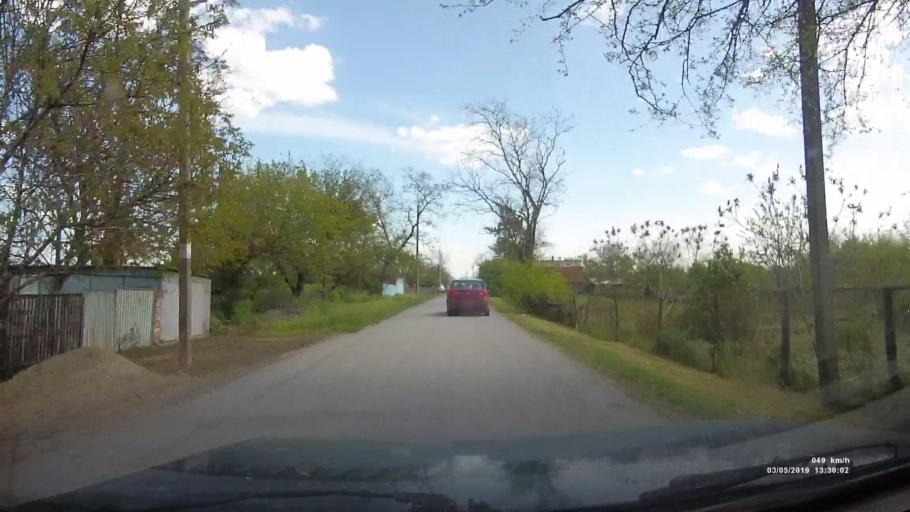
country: RU
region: Rostov
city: Ust'-Donetskiy
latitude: 47.5810
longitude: 40.8483
